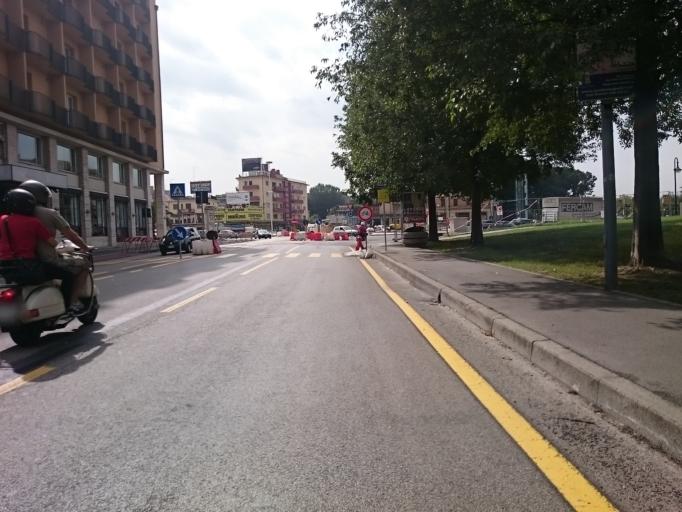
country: IT
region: Veneto
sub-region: Provincia di Padova
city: Padova
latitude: 45.4097
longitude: 11.9021
